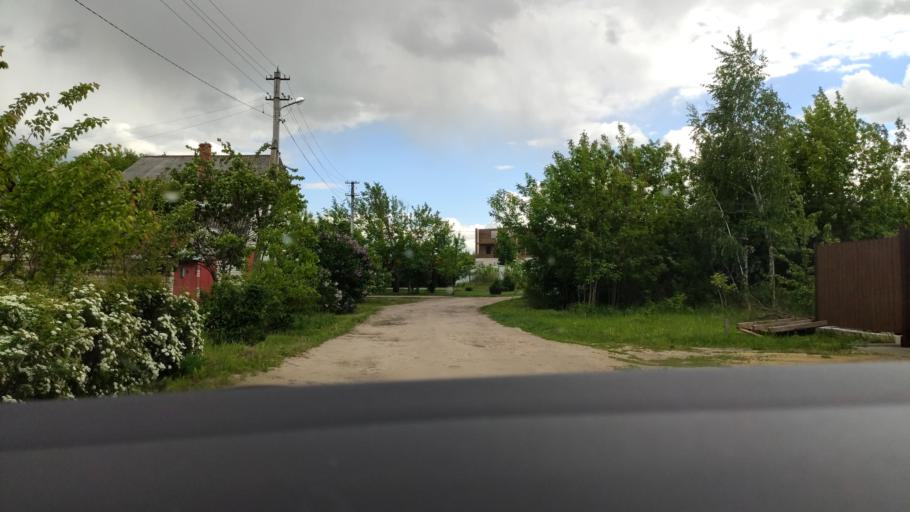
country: RU
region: Voronezj
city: Somovo
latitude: 51.6819
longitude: 39.3126
